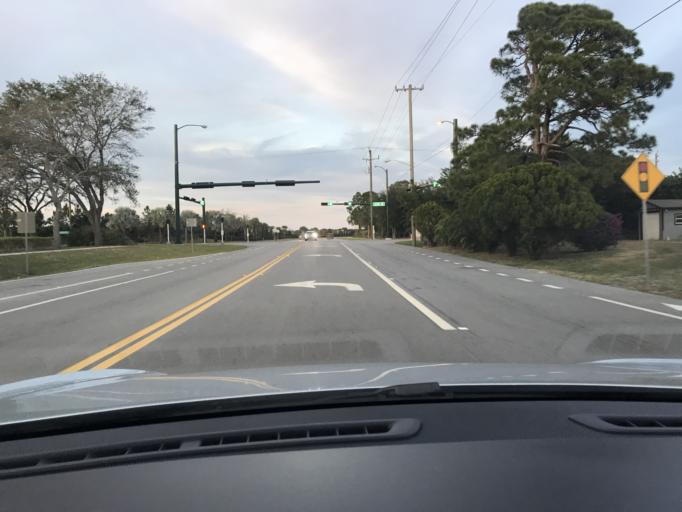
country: US
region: Florida
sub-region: Indian River County
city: Gifford
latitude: 27.6818
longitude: -80.4295
